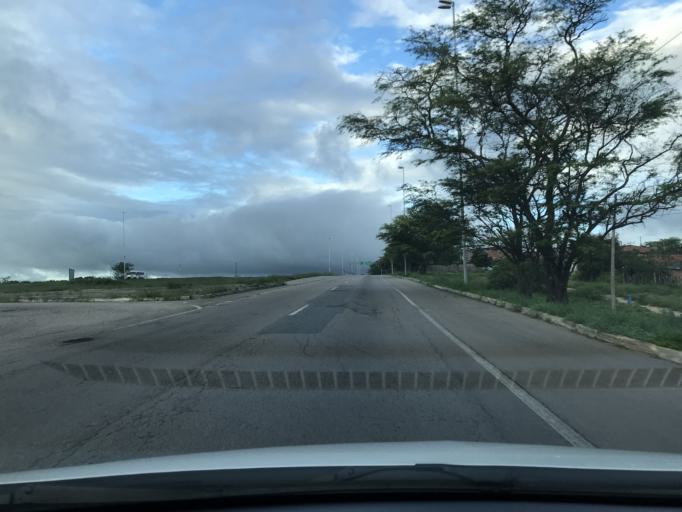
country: BR
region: Pernambuco
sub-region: Bezerros
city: Bezerros
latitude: -8.2991
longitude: -35.8557
